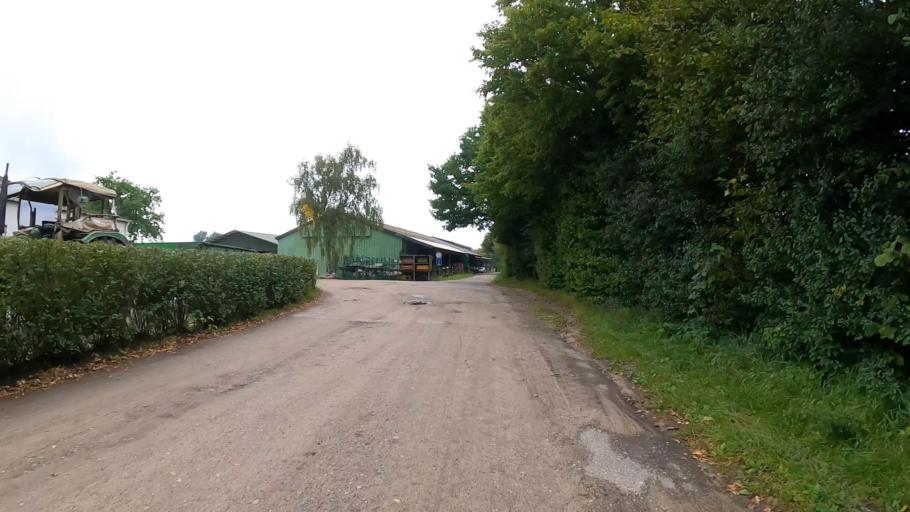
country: DE
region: Schleswig-Holstein
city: Rellingen
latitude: 53.6339
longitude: 9.8276
